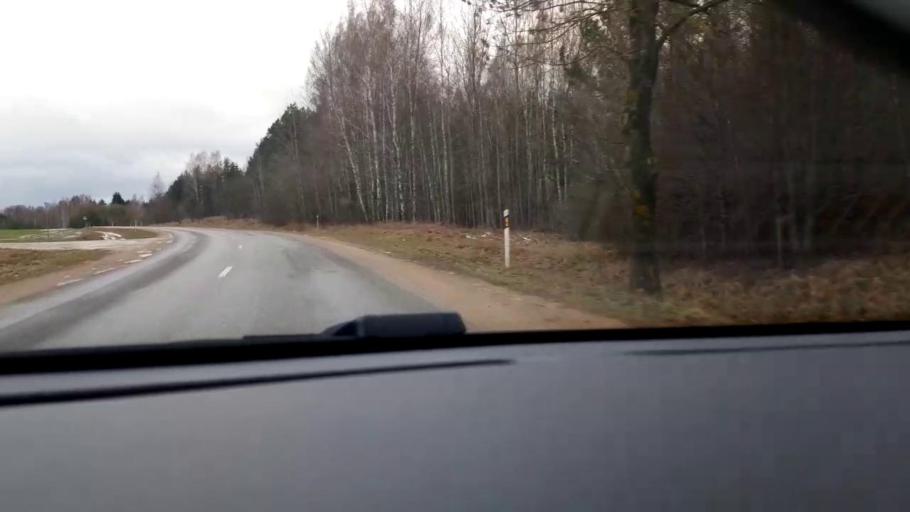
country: LT
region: Vilnius County
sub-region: Vilnius
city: Fabijoniskes
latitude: 54.8576
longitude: 25.2640
